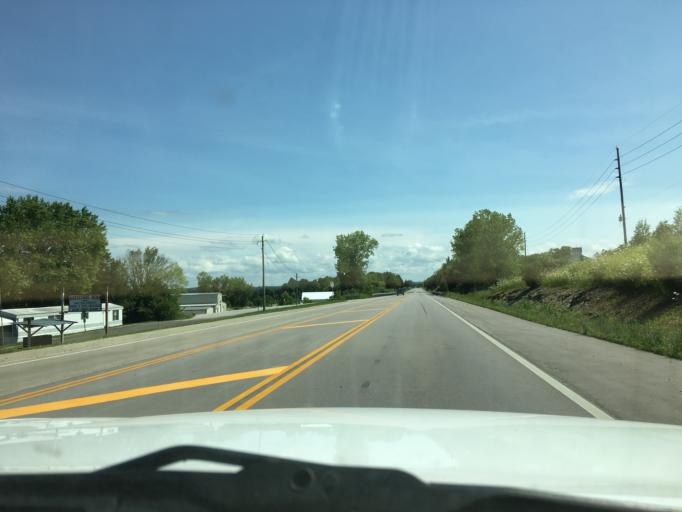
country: US
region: Missouri
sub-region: Franklin County
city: Union
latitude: 38.4808
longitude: -91.0053
